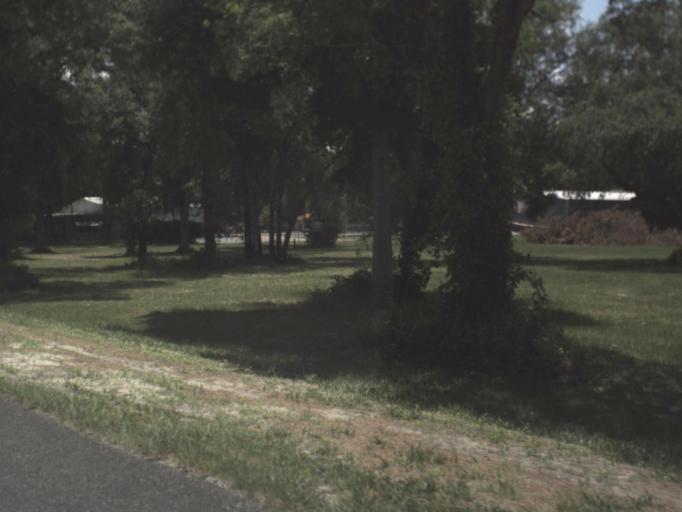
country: US
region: Florida
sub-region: Levy County
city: Manatee Road
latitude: 29.5524
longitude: -82.9014
